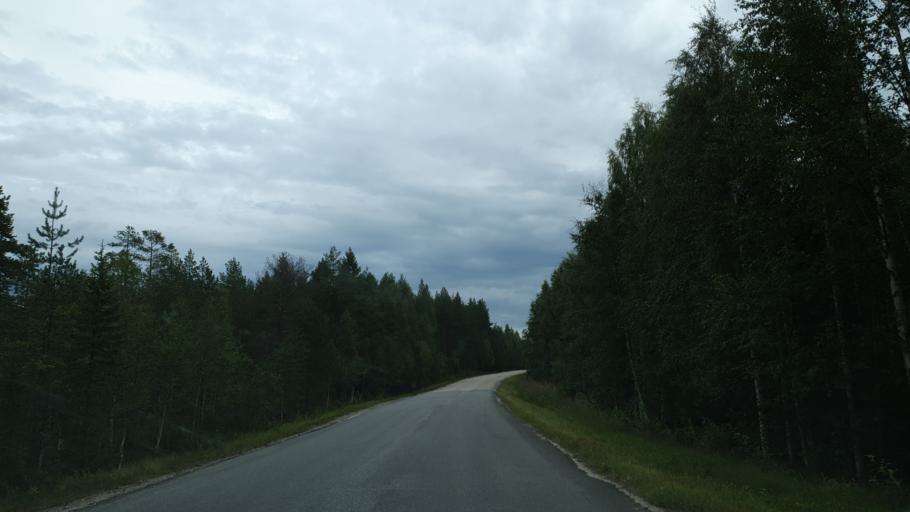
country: FI
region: Kainuu
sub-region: Kehys-Kainuu
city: Kuhmo
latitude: 64.3572
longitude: 29.1951
